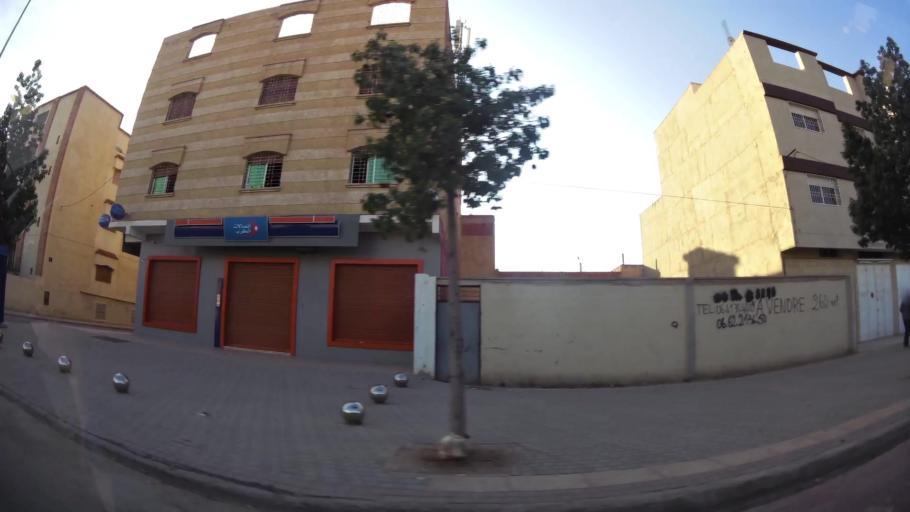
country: MA
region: Oriental
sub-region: Oujda-Angad
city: Oujda
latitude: 34.7050
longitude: -1.8950
